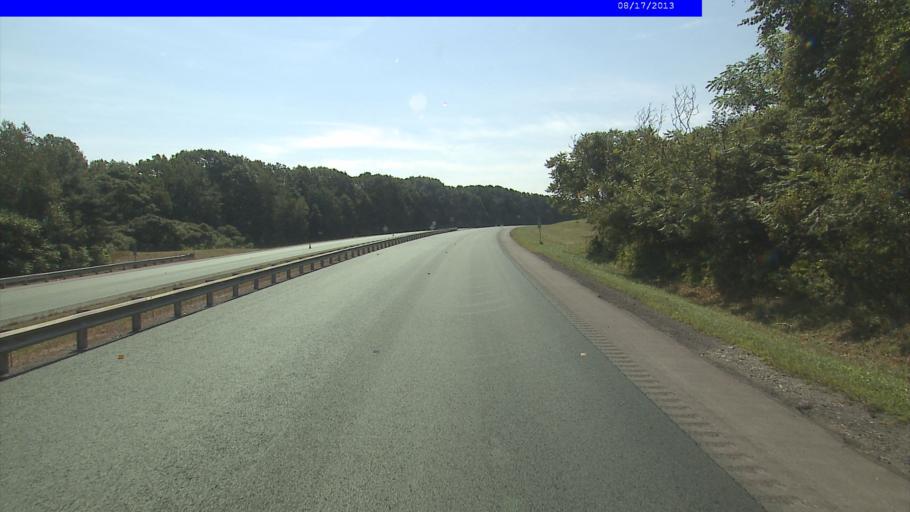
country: US
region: New Hampshire
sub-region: Cheshire County
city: Chesterfield
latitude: 42.9435
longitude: -72.5296
